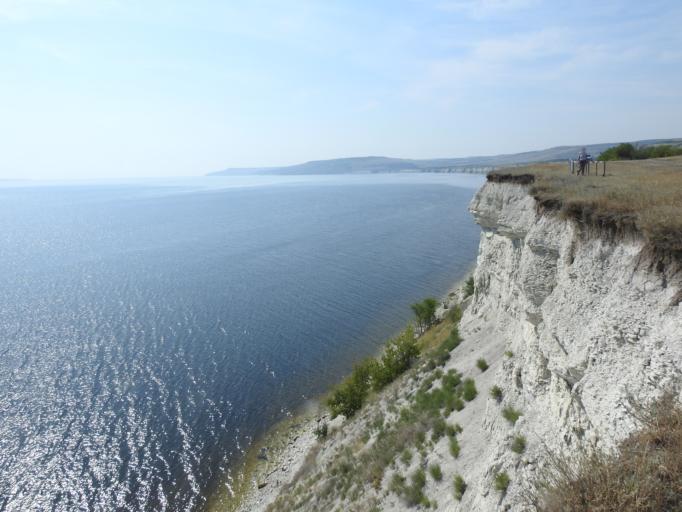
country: RU
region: Saratov
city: Kamenskiy
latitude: 50.6488
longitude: 45.6472
